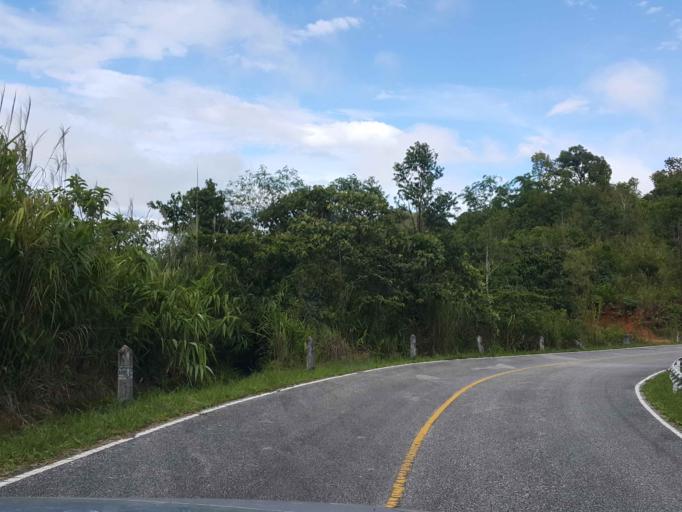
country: TH
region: Tak
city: Tak
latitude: 16.7805
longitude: 98.9311
